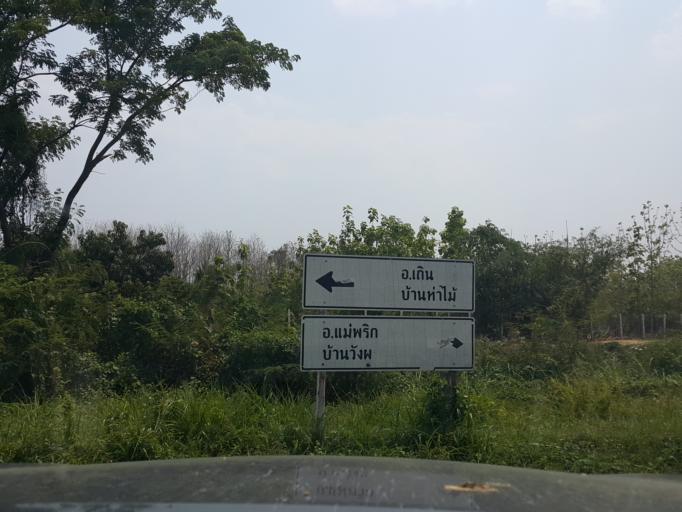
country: TH
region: Lampang
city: Mae Phrik
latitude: 17.5131
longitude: 99.1414
